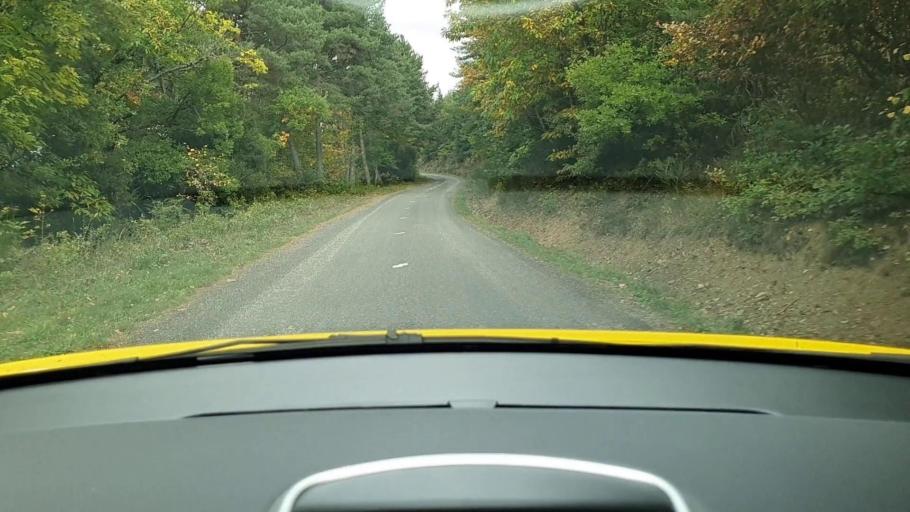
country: FR
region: Languedoc-Roussillon
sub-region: Departement de la Lozere
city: Meyrueis
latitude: 44.0677
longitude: 3.4063
